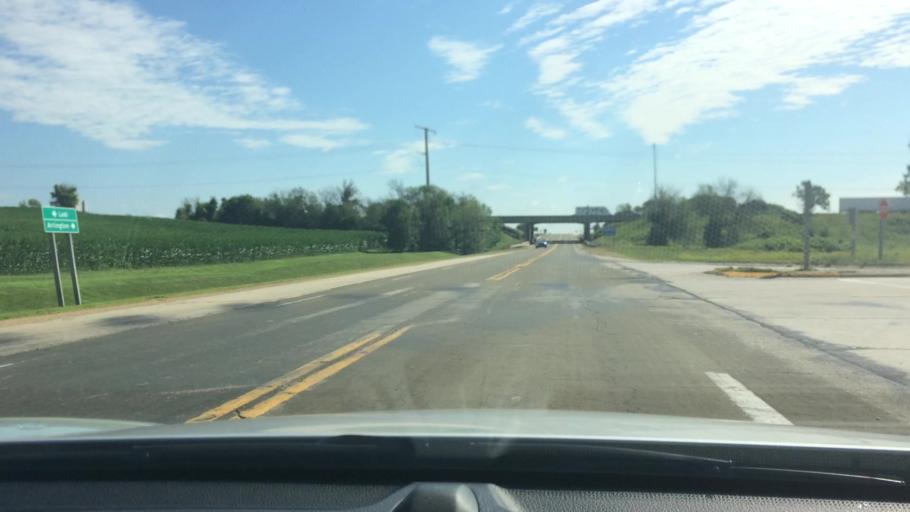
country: US
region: Wisconsin
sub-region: Columbia County
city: Lodi
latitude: 43.3343
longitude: -89.4562
